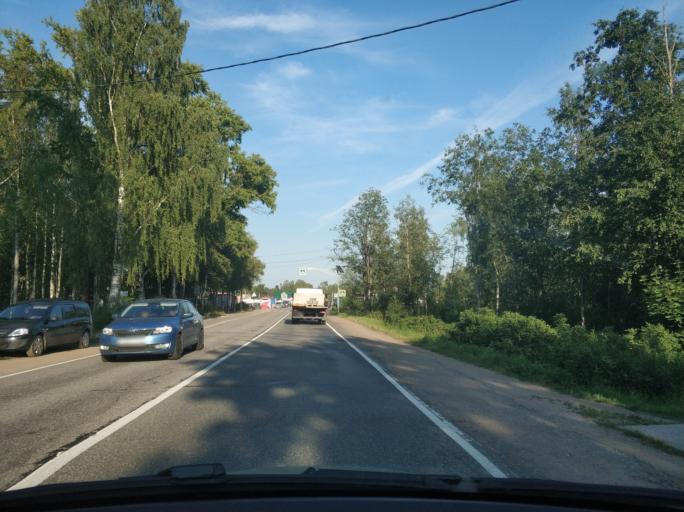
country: RU
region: Leningrad
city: Borisova Griva
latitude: 60.0946
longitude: 30.9726
